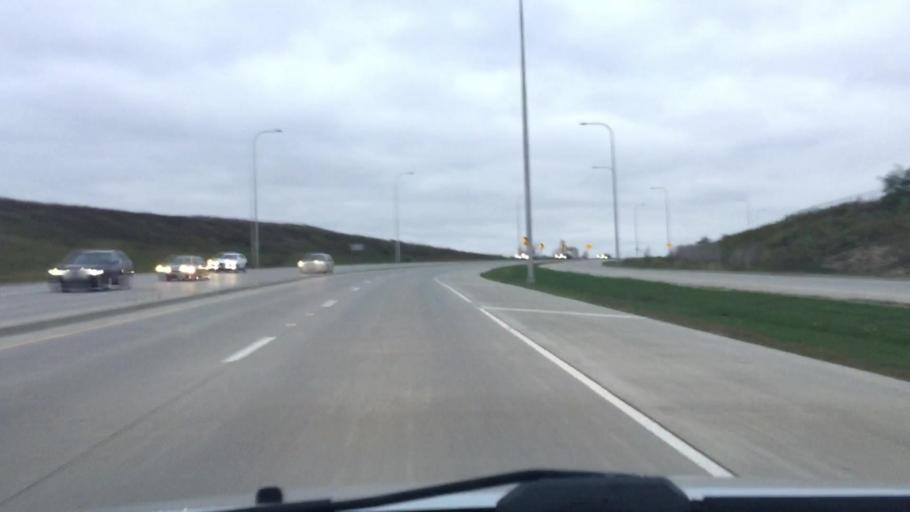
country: US
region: Illinois
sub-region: McHenry County
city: Algonquin
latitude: 42.1742
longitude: -88.2943
